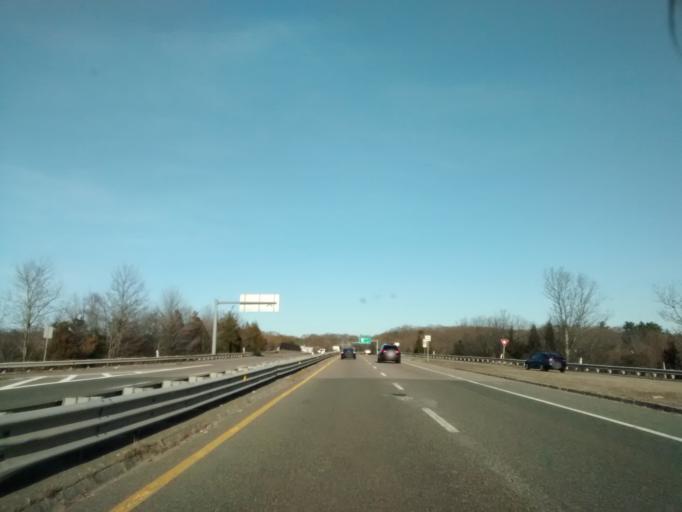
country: US
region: Massachusetts
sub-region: Norfolk County
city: Avon
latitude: 42.1254
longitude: -71.0645
